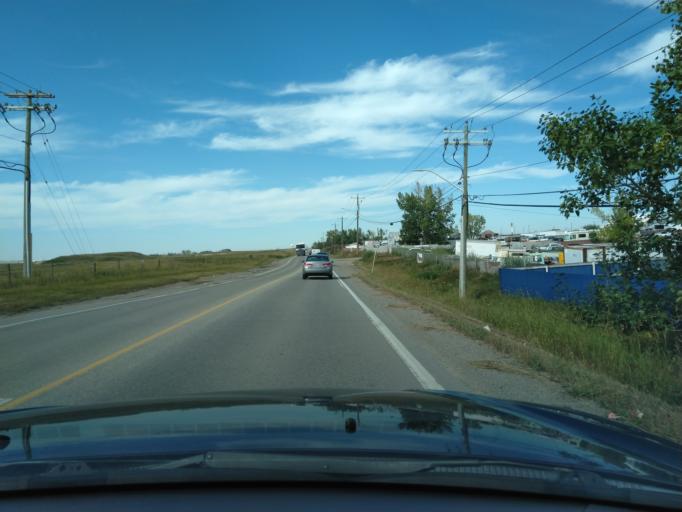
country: CA
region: Alberta
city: Calgary
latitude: 51.1140
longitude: -113.9817
